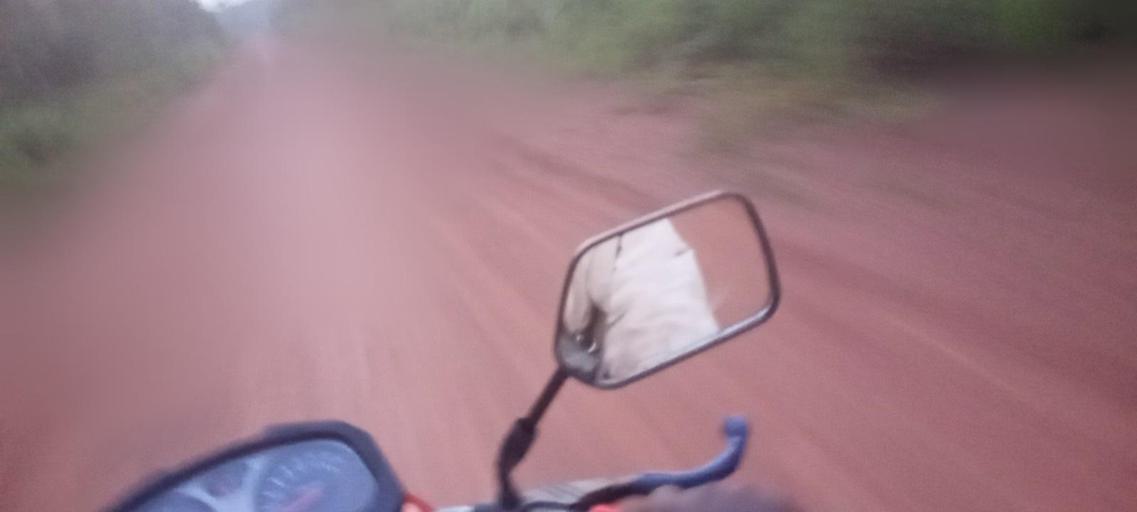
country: CD
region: Eastern Province
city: Kisangani
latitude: -0.1639
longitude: 25.6848
